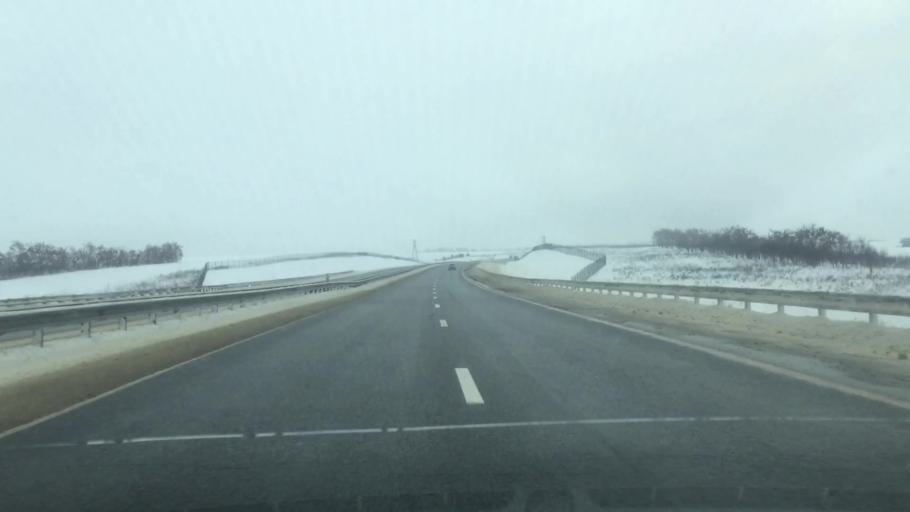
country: RU
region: Tula
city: Yefremov
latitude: 53.1490
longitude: 38.2501
